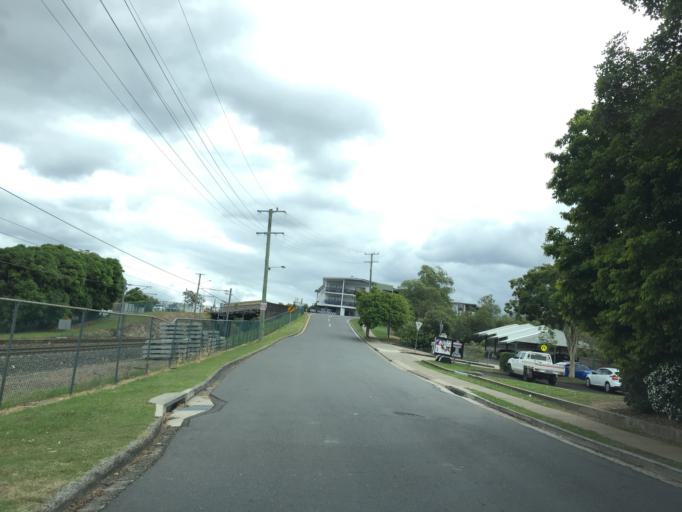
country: AU
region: Queensland
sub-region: Brisbane
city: Grange
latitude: -27.4274
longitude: 153.0054
